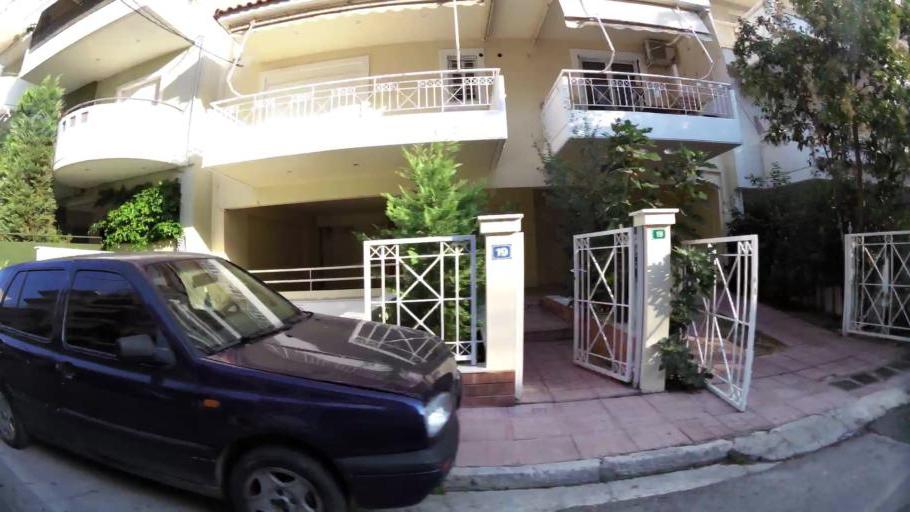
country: GR
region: Attica
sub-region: Nomarchia Athinas
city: Petroupolis
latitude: 38.0485
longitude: 23.6820
